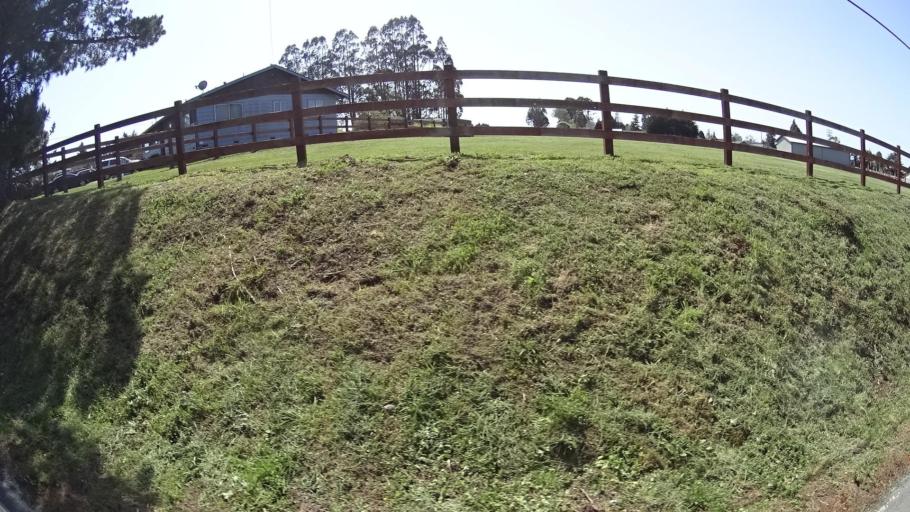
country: US
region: California
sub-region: Humboldt County
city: Hydesville
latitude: 40.5576
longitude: -124.1231
